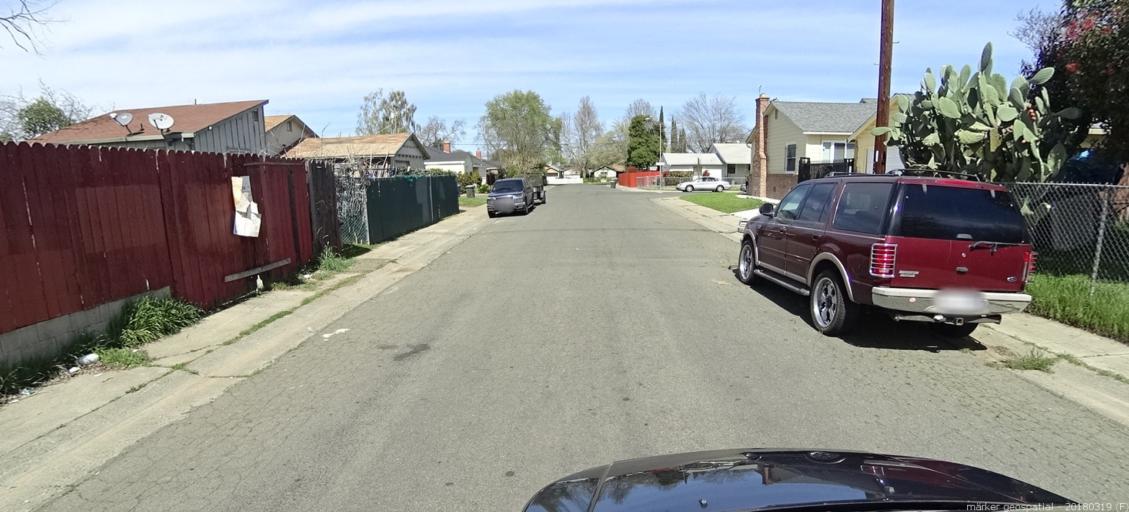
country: US
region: California
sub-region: Sacramento County
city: Parkway
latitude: 38.5176
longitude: -121.4529
